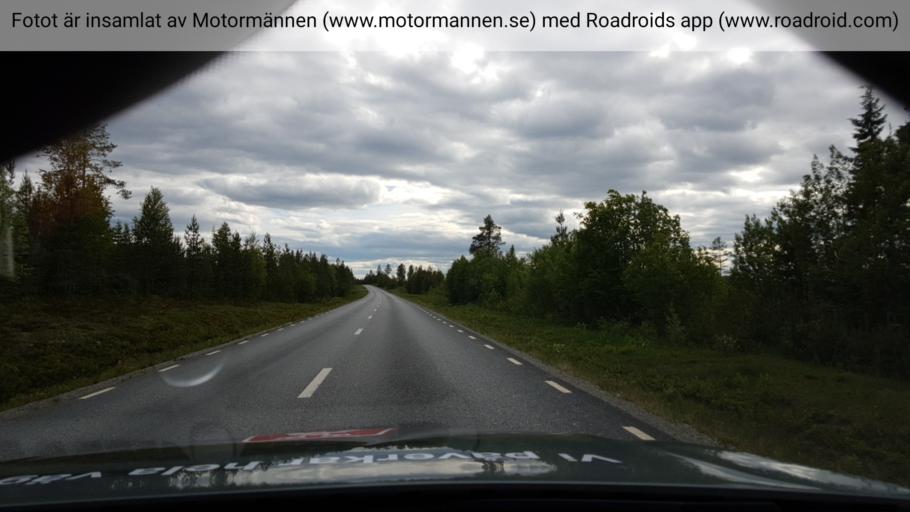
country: SE
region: Jaemtland
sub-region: Stroemsunds Kommun
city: Stroemsund
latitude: 63.9804
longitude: 15.4937
